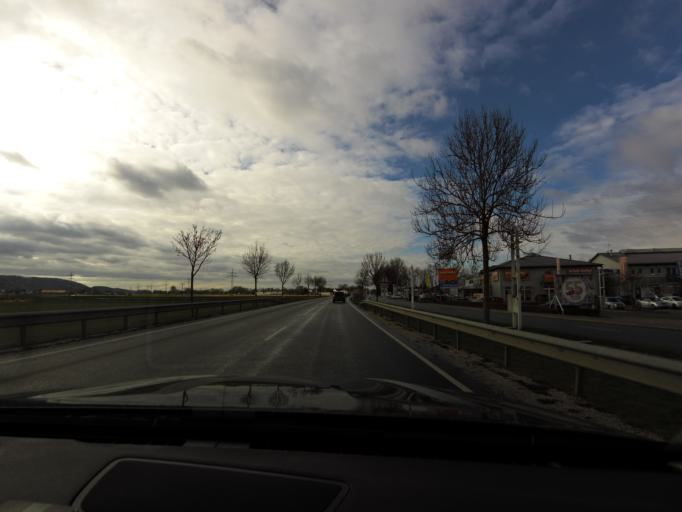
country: DE
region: Bavaria
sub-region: Lower Bavaria
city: Eching
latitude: 48.4885
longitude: 12.0231
